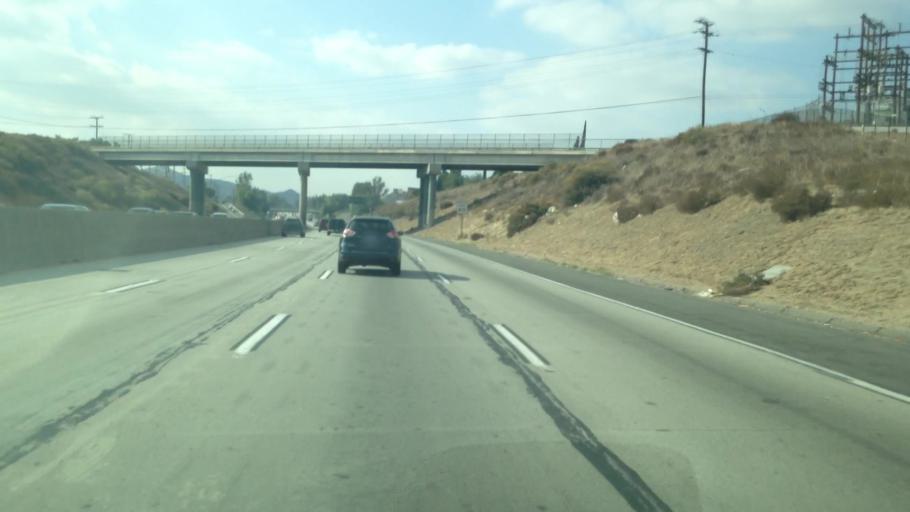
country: US
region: California
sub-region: Riverside County
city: Rubidoux
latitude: 34.0053
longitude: -117.3915
